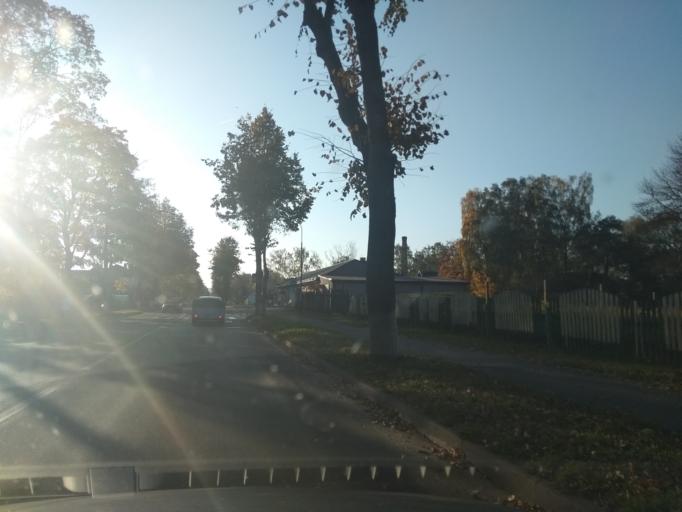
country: BY
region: Grodnenskaya
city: Vawkavysk
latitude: 53.1541
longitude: 24.4425
